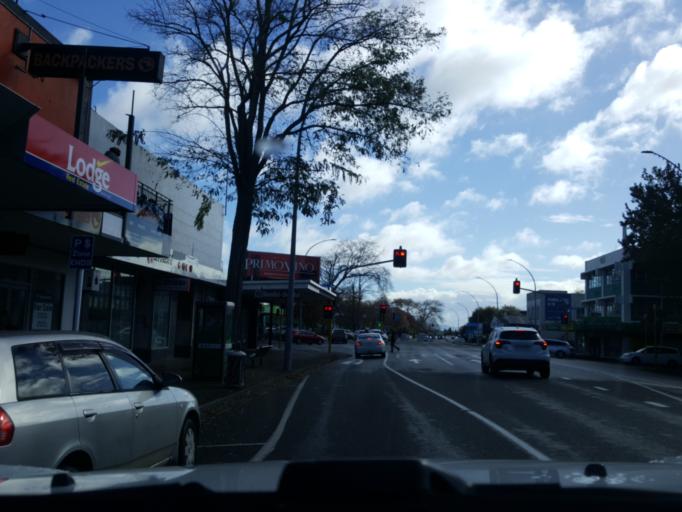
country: NZ
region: Waikato
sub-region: Hamilton City
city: Hamilton
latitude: -37.7802
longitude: 175.2765
